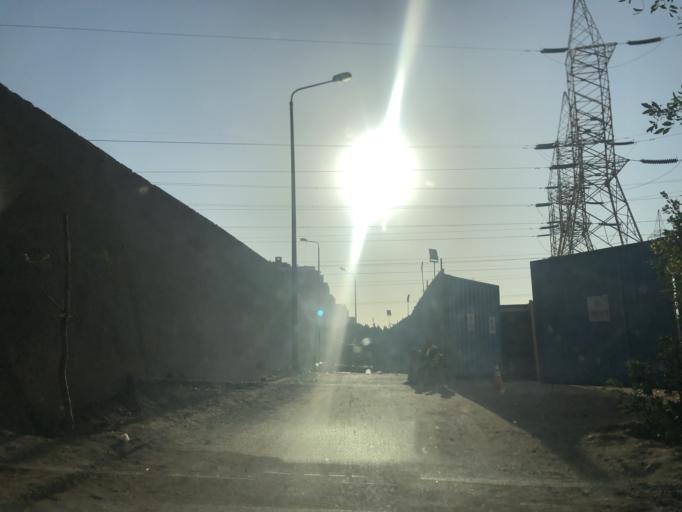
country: EG
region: Al Jizah
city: Al Jizah
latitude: 29.9883
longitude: 31.0970
